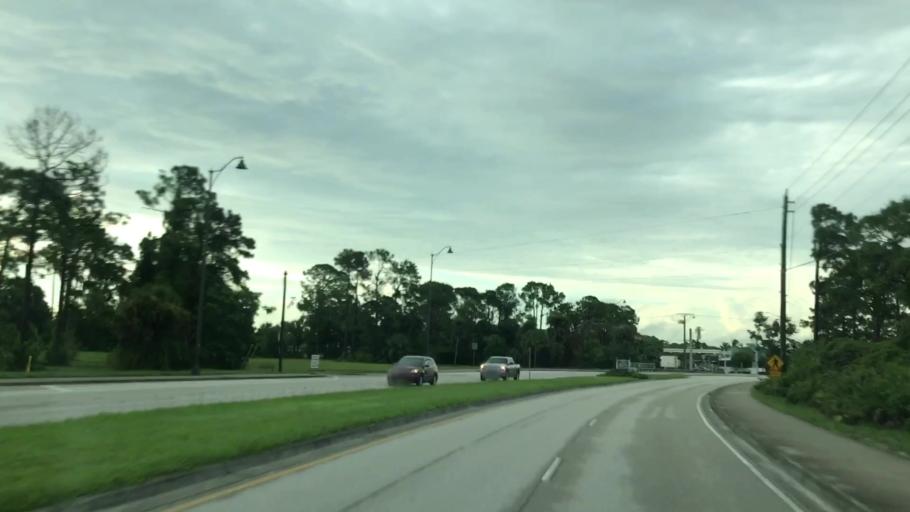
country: US
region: Florida
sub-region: Lee County
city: Bonita Springs
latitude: 26.3528
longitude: -81.7802
